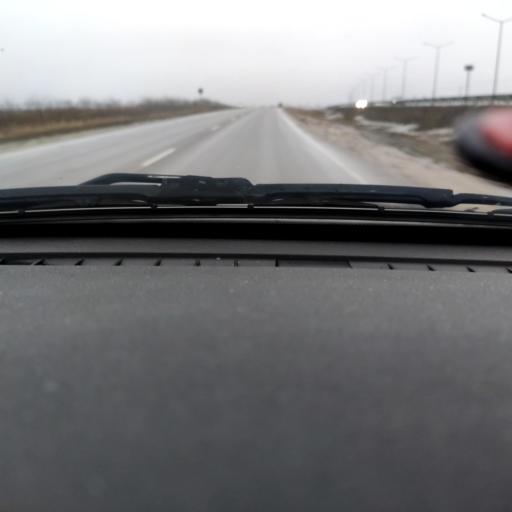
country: RU
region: Voronezj
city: Novaya Usman'
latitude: 51.5906
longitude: 39.3717
